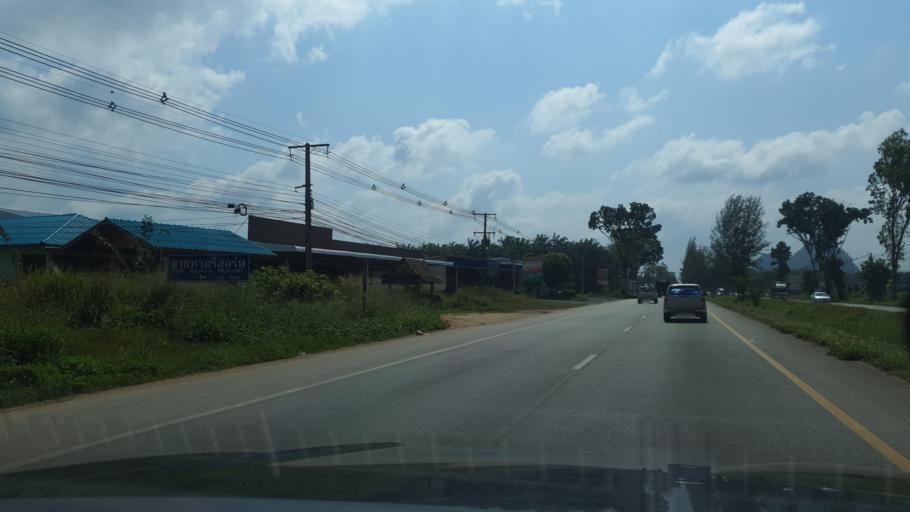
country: TH
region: Chumphon
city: Lang Suan
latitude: 10.0261
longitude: 99.0679
